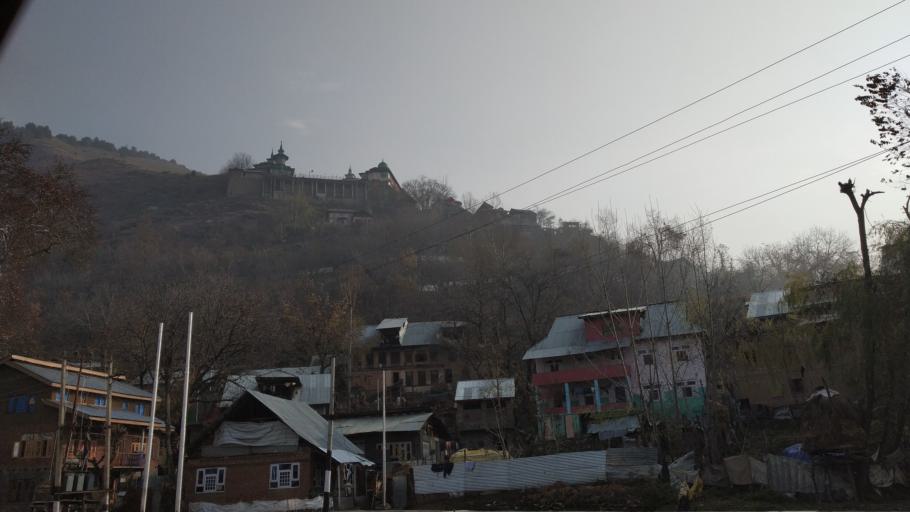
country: IN
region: Kashmir
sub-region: Anantnag
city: Pahalgam
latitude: 33.8652
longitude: 75.2791
